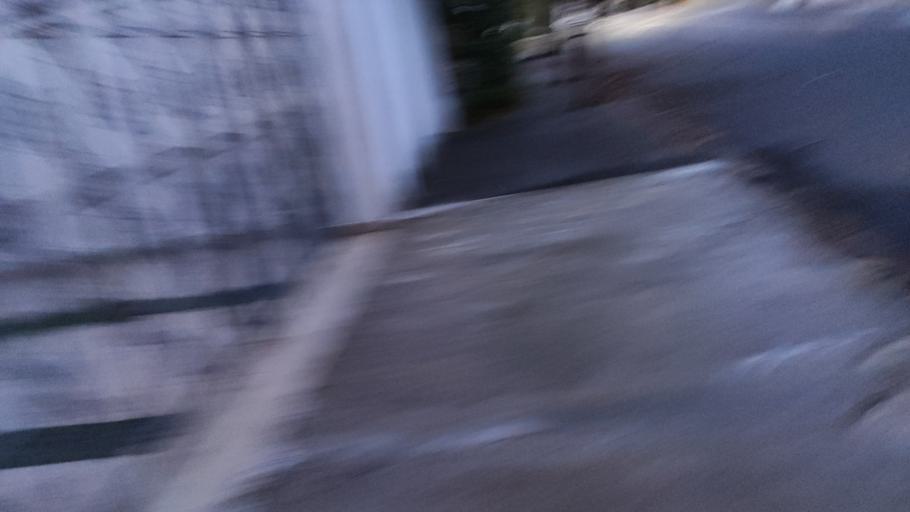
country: BR
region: Sao Paulo
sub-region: Sao Jose Dos Campos
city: Sao Jose dos Campos
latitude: -23.2003
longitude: -45.9077
